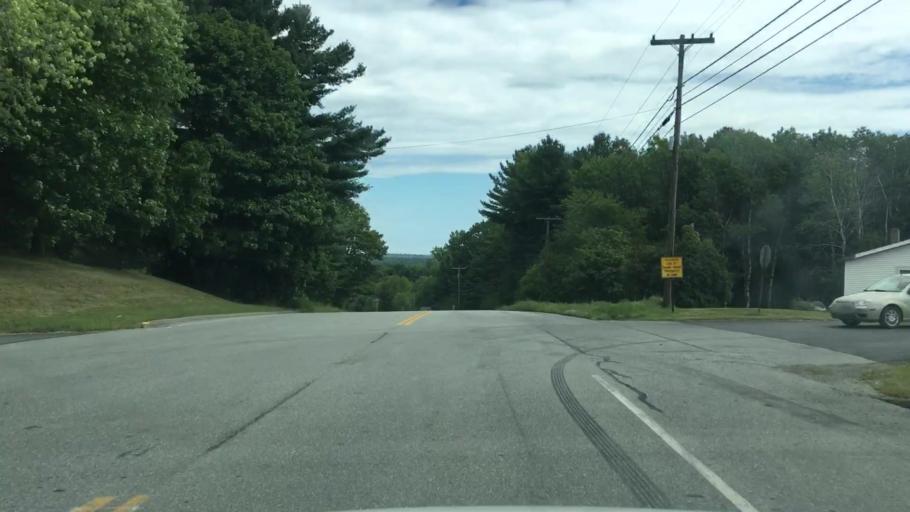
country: US
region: Maine
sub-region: Piscataquis County
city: Milo
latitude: 45.2447
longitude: -69.0084
